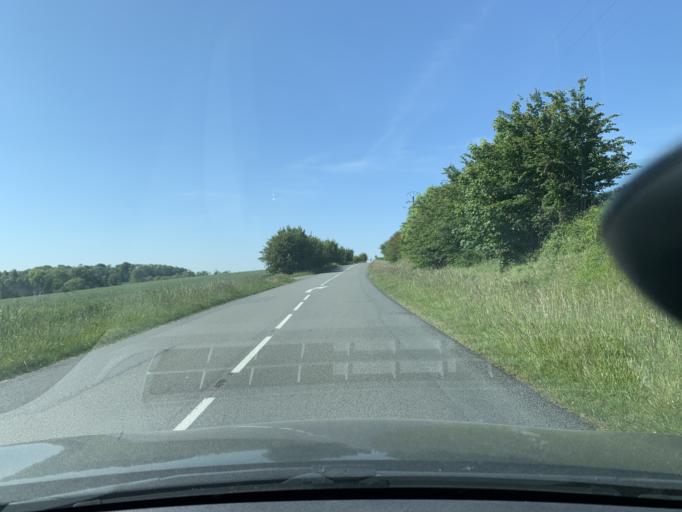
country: FR
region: Nord-Pas-de-Calais
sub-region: Departement du Nord
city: Masnieres
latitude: 50.0820
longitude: 3.2169
